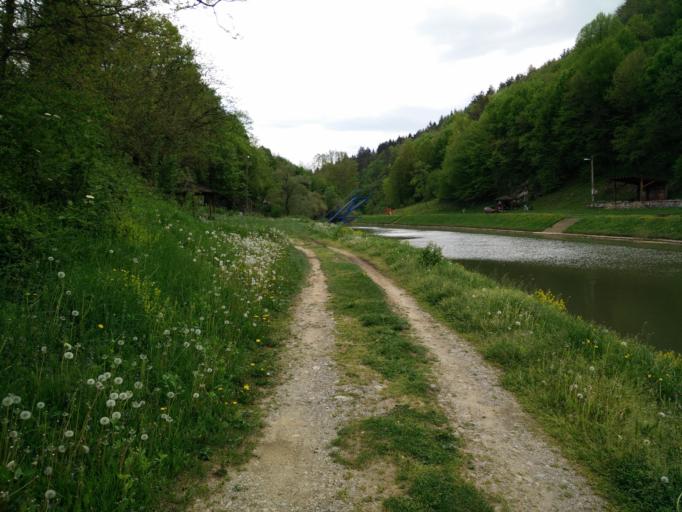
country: HR
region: Karlovacka
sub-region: Grad Karlovac
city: Slunj
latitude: 45.1213
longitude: 15.5899
